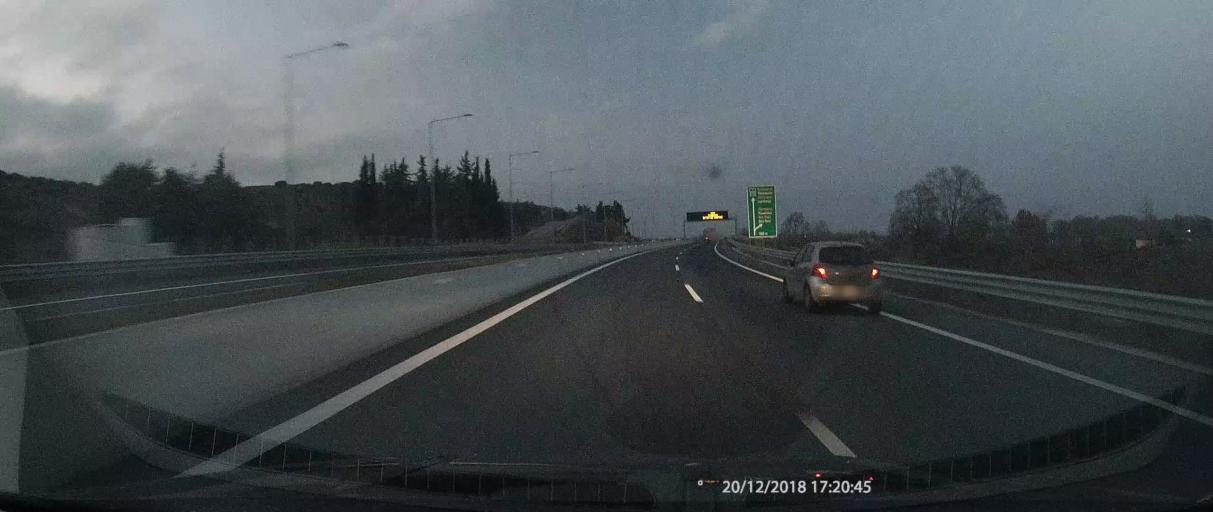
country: GR
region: Thessaly
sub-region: Nomos Larisis
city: Pyrgetos
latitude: 39.9703
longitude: 22.6398
